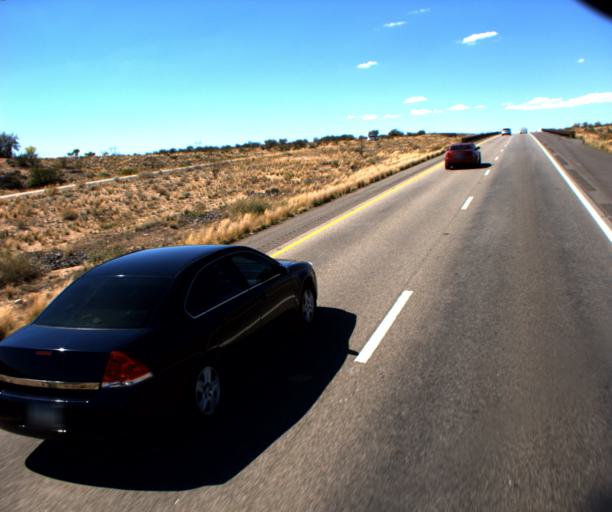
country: US
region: Arizona
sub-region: Mohave County
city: Kingman
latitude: 34.8600
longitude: -113.6409
